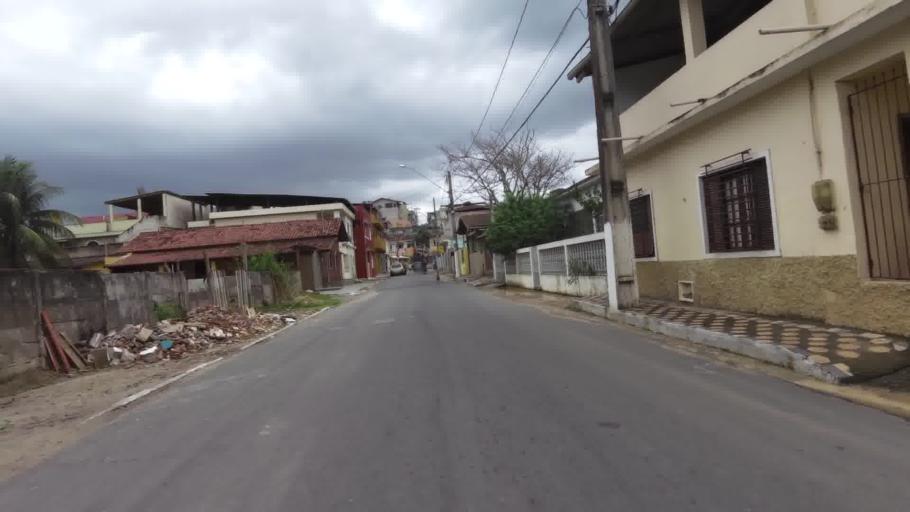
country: BR
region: Espirito Santo
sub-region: Marataizes
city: Marataizes
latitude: -21.0449
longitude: -40.8304
